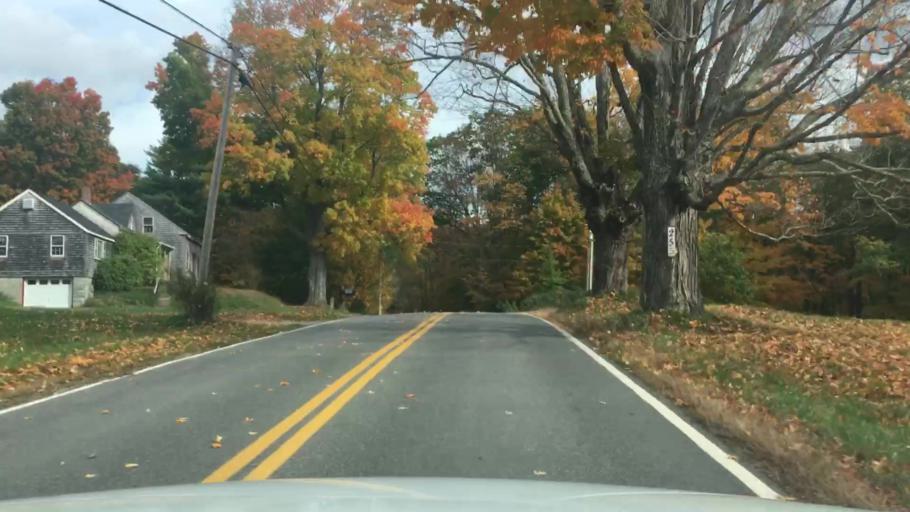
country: US
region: Maine
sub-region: Knox County
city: Hope
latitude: 44.2802
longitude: -69.1249
